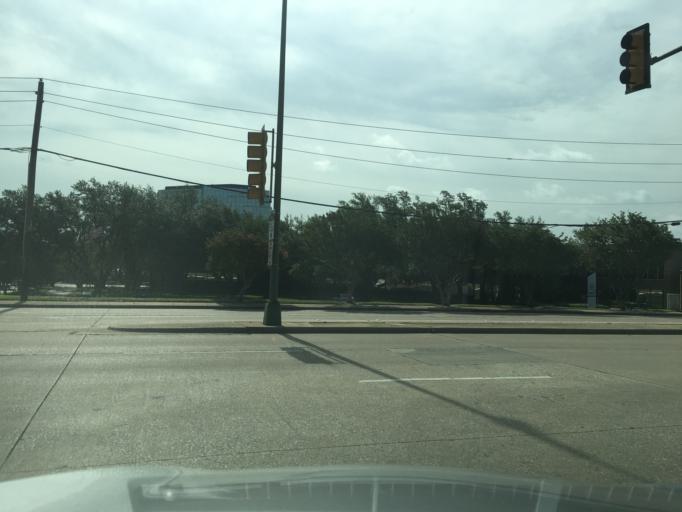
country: US
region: Texas
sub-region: Dallas County
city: Addison
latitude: 32.9226
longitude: -96.7891
